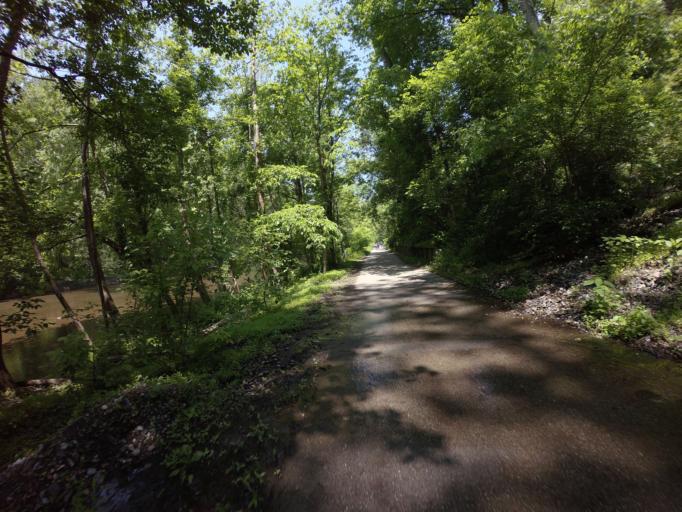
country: US
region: Maryland
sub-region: Howard County
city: Ilchester
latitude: 39.2428
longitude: -76.7505
